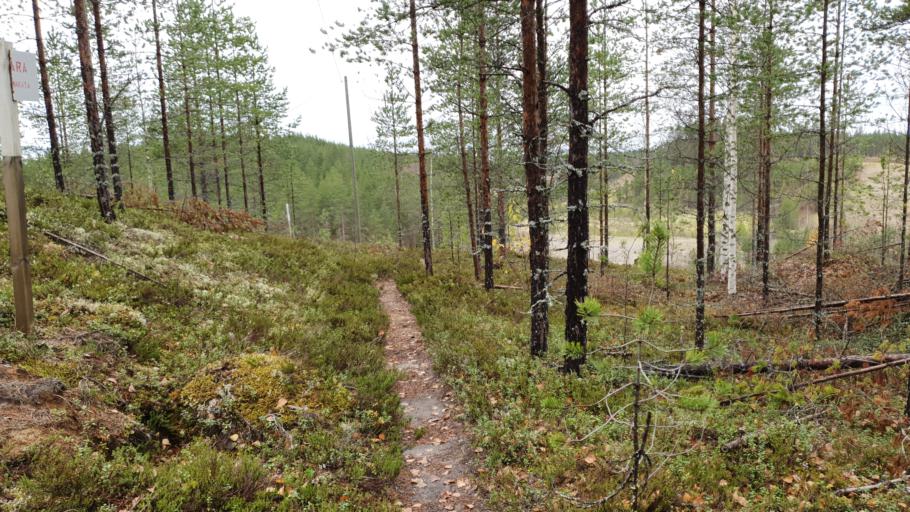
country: FI
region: Kainuu
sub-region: Kehys-Kainuu
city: Kuhmo
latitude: 64.1524
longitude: 29.3906
